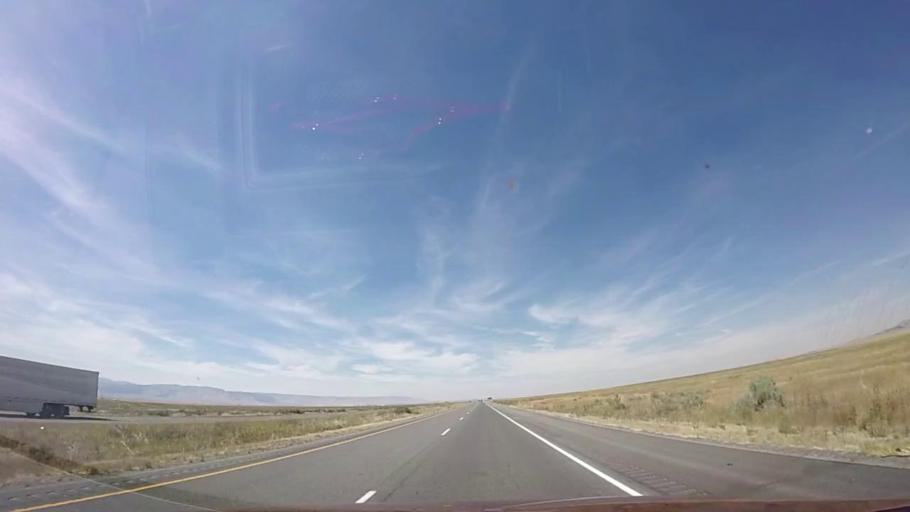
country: US
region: Idaho
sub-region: Power County
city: American Falls
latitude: 42.3017
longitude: -113.1805
